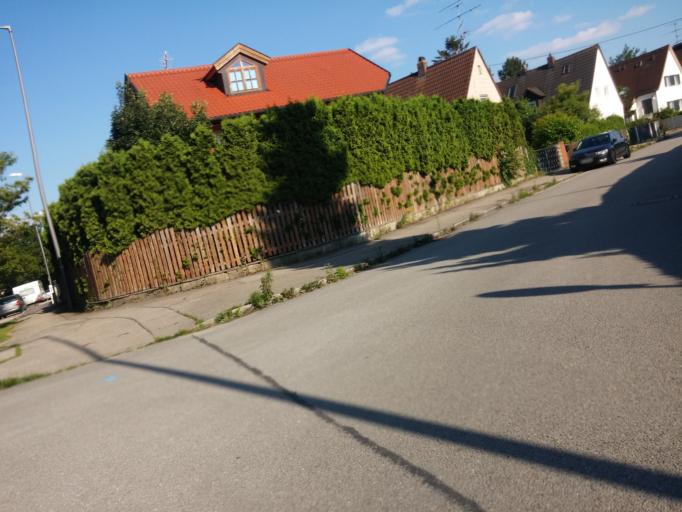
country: DE
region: Bavaria
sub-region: Upper Bavaria
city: Neubiberg
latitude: 48.1303
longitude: 11.6682
